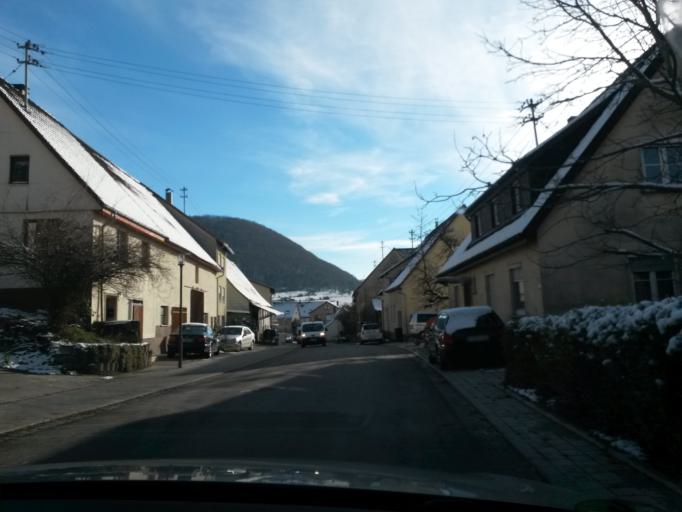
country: DE
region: Baden-Wuerttemberg
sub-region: Regierungsbezirk Stuttgart
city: Gingen an der Fils
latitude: 48.6301
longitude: 9.7613
